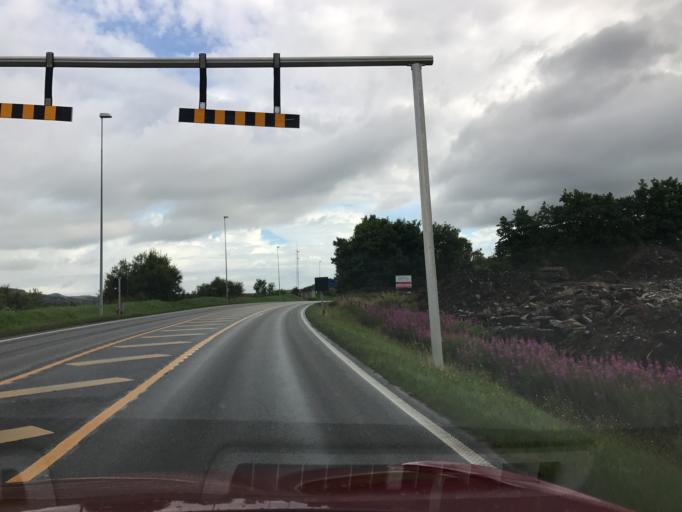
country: NO
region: Rogaland
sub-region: Rennesoy
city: Vikevag
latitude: 59.0695
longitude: 5.6734
